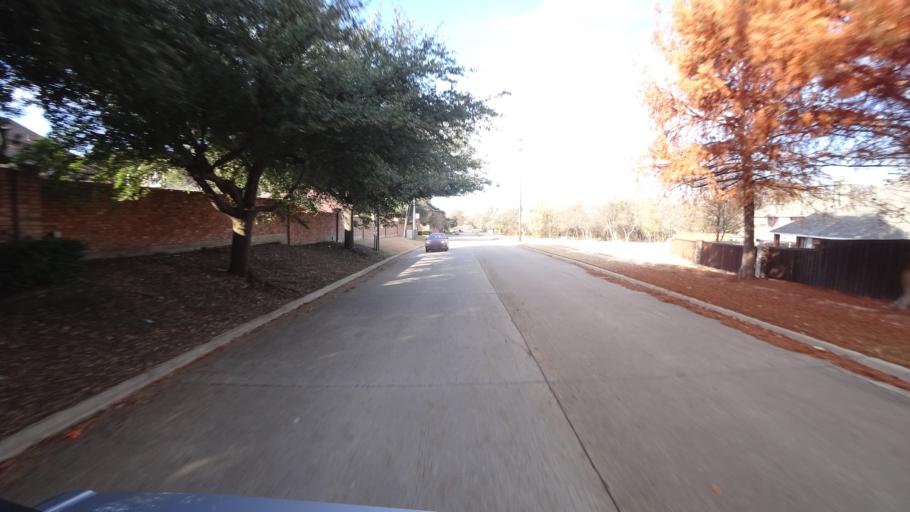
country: US
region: Texas
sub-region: Collin County
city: McKinney
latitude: 33.2047
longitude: -96.6522
